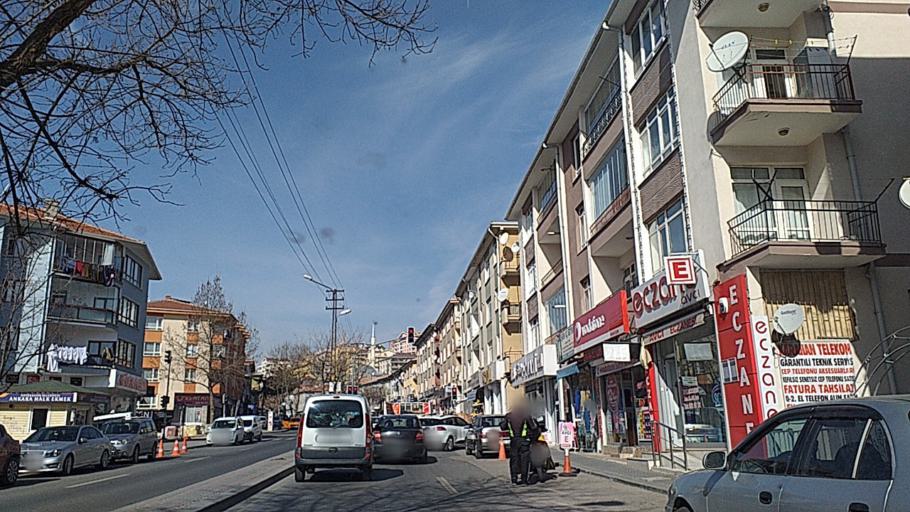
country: TR
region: Ankara
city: Ankara
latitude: 39.9840
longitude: 32.8320
